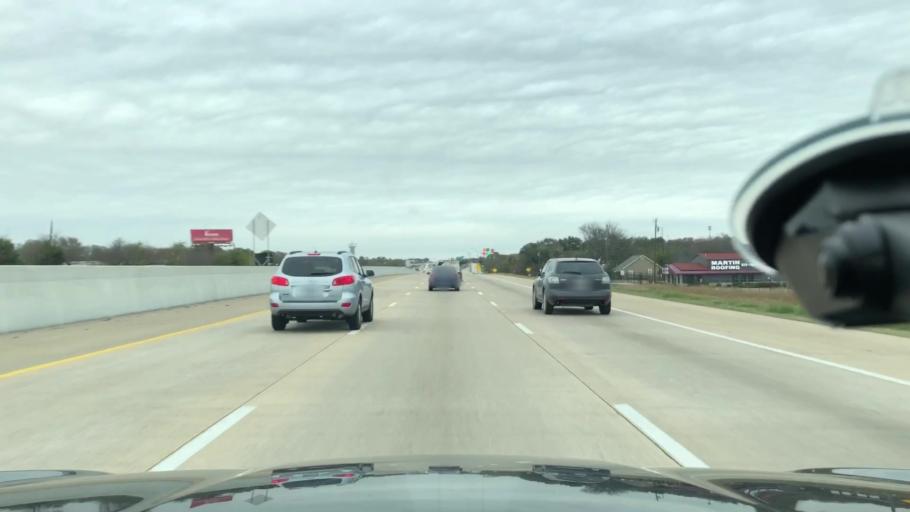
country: US
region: Texas
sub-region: Ellis County
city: Red Oak
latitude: 32.5069
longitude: -96.8220
